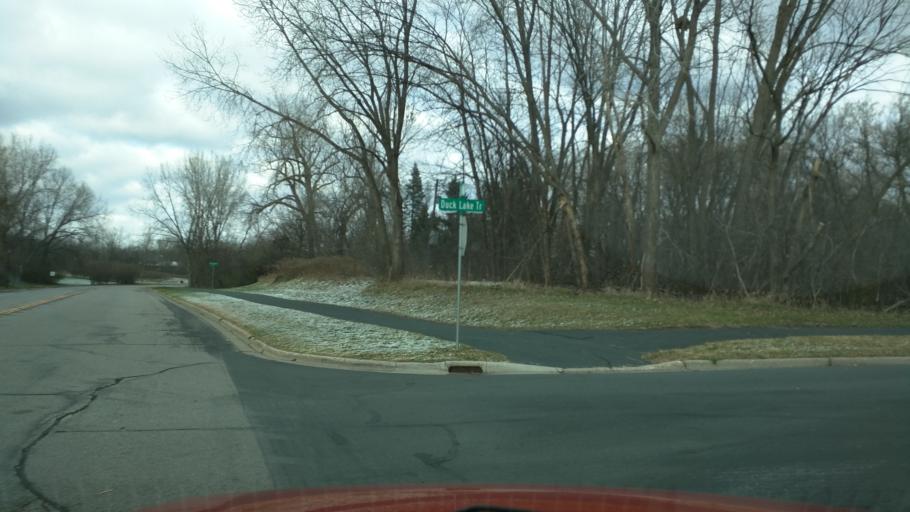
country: US
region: Minnesota
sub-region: Carver County
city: Chanhassen
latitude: 44.8769
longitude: -93.5136
